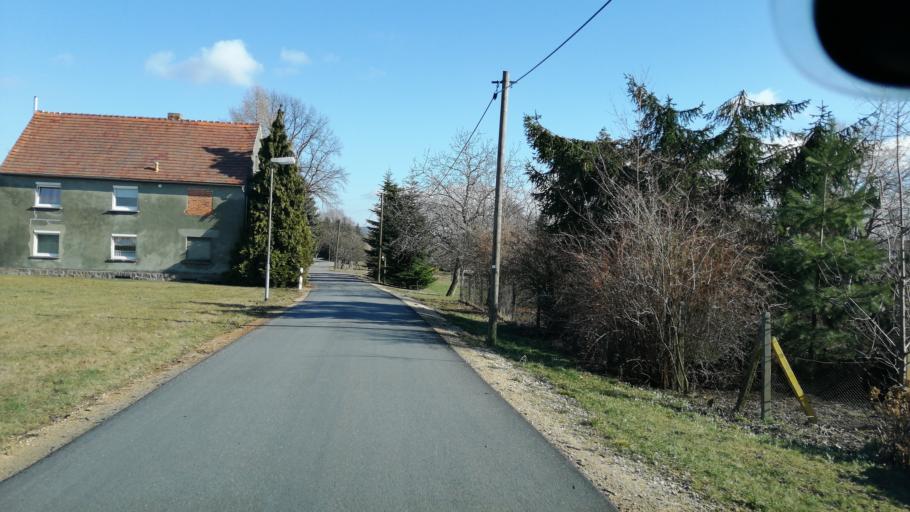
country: DE
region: Saxony
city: Weissenberg
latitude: 51.1677
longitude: 14.7155
